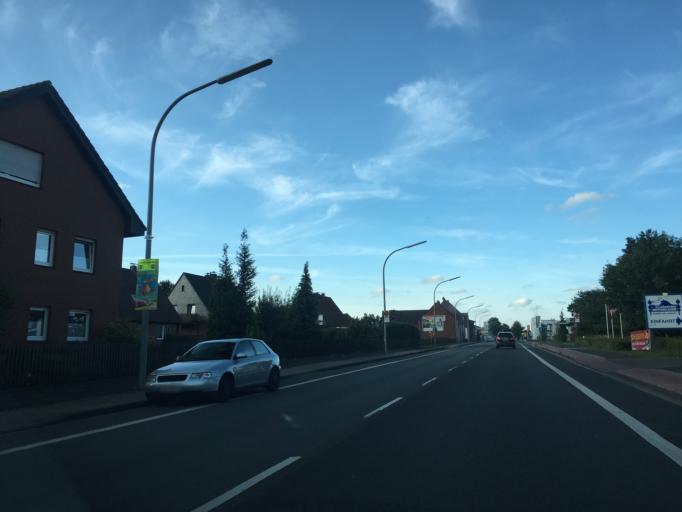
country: DE
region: North Rhine-Westphalia
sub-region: Regierungsbezirk Munster
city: Dulmen
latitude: 51.8370
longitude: 7.2850
